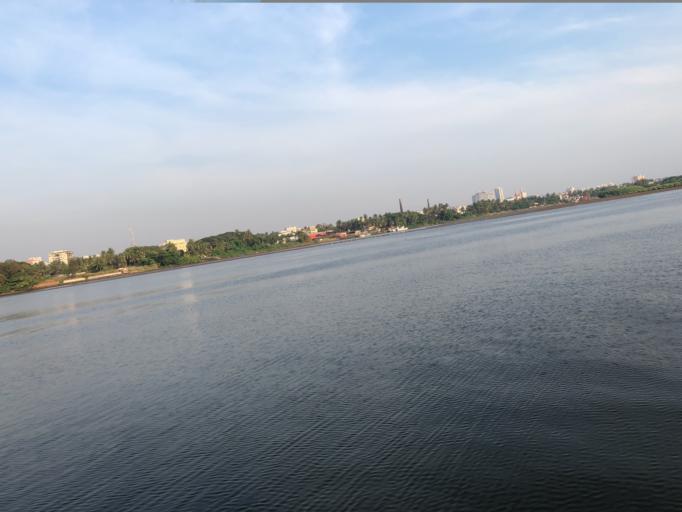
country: IN
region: Karnataka
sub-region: Dakshina Kannada
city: Mangalore
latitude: 12.8830
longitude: 74.8192
